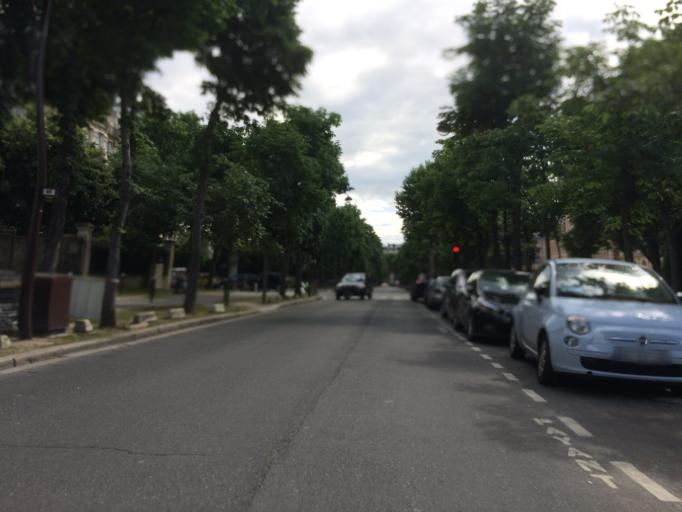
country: FR
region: Ile-de-France
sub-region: Departement des Hauts-de-Seine
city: Neuilly-sur-Seine
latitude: 48.8870
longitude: 2.2750
